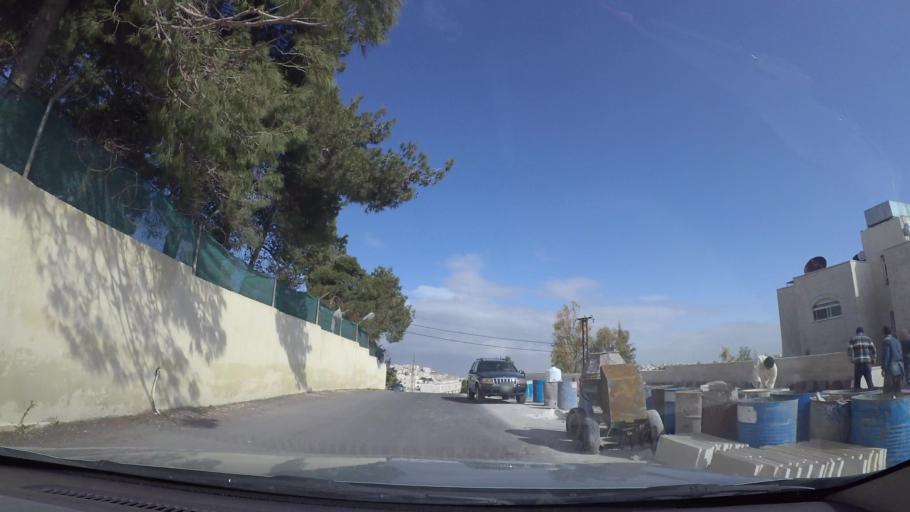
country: JO
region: Amman
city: Al Jubayhah
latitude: 32.0062
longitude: 35.8442
